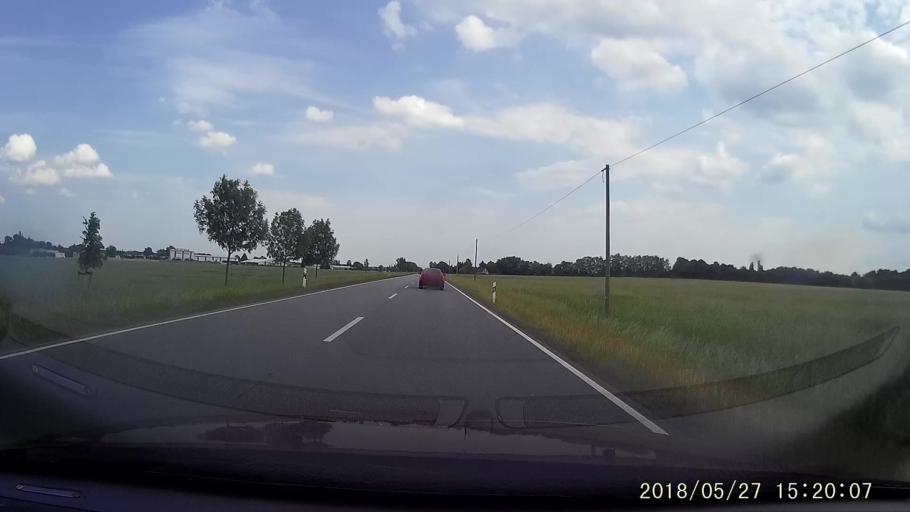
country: DE
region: Saxony
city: Kodersdorf
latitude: 51.2500
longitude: 14.8821
